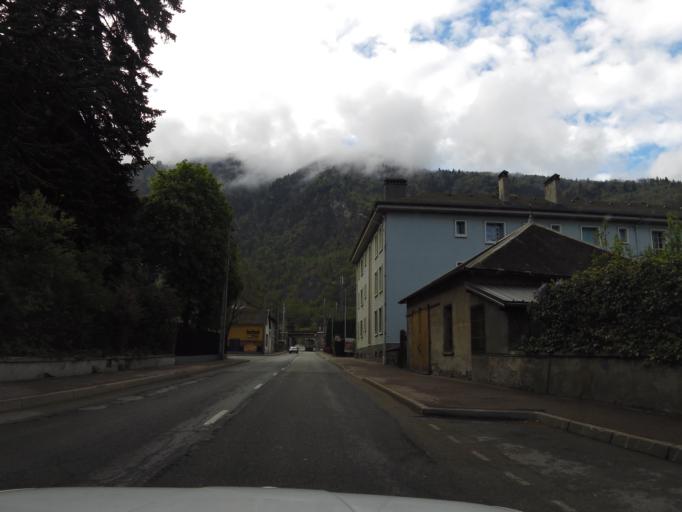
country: FR
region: Rhone-Alpes
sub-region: Departement de la Savoie
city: Saint-Michel-de-Maurienne
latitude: 45.2129
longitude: 6.4776
